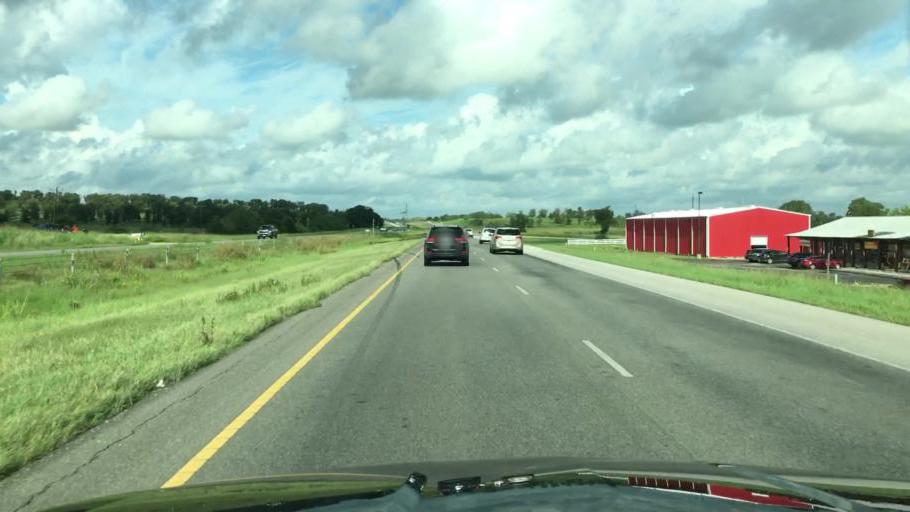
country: US
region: Texas
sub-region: Travis County
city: Garfield
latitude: 30.1660
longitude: -97.5106
